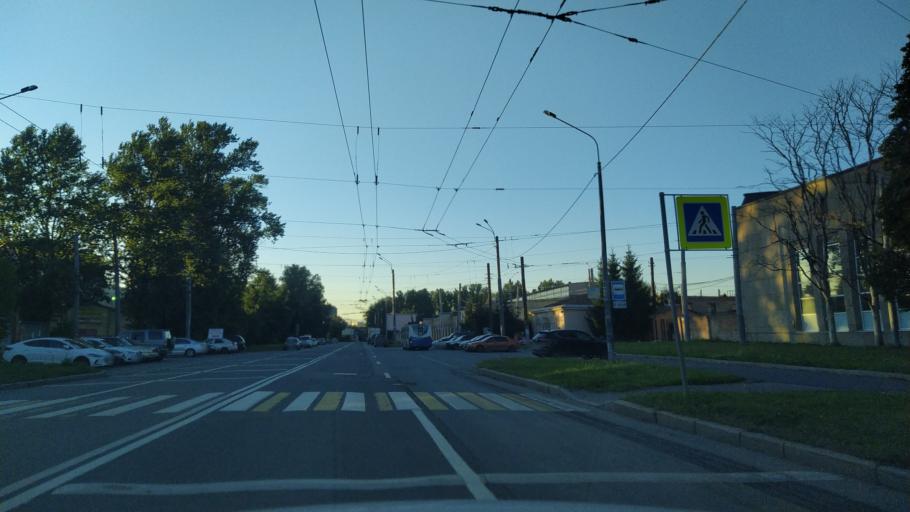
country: RU
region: Leningrad
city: Finlyandskiy
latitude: 59.9679
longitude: 30.3662
